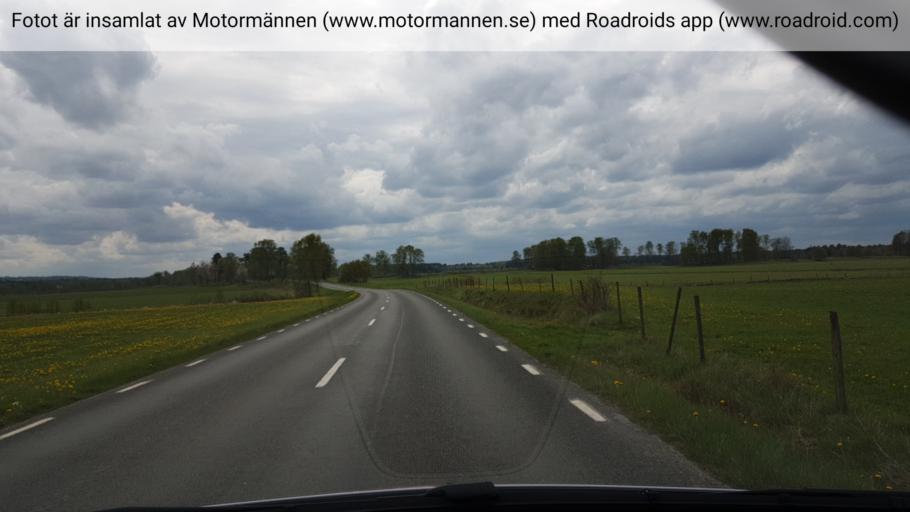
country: SE
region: Vaestra Goetaland
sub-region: Falkopings Kommun
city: Falkoeping
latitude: 58.2546
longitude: 13.4467
